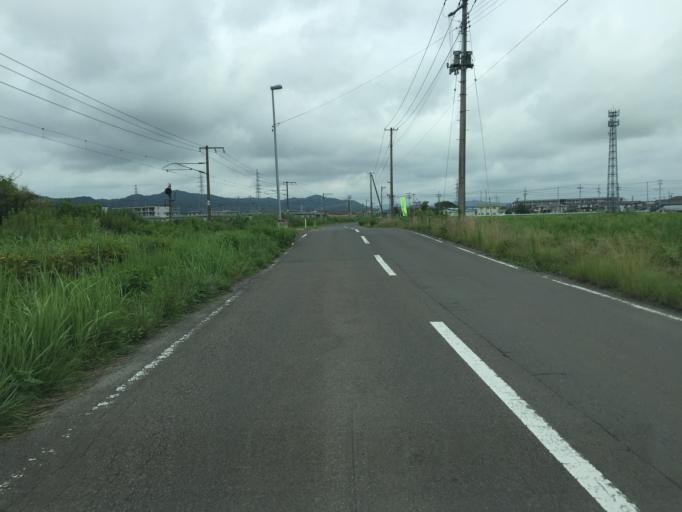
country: JP
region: Miyagi
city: Watari
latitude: 38.0309
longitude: 140.8681
